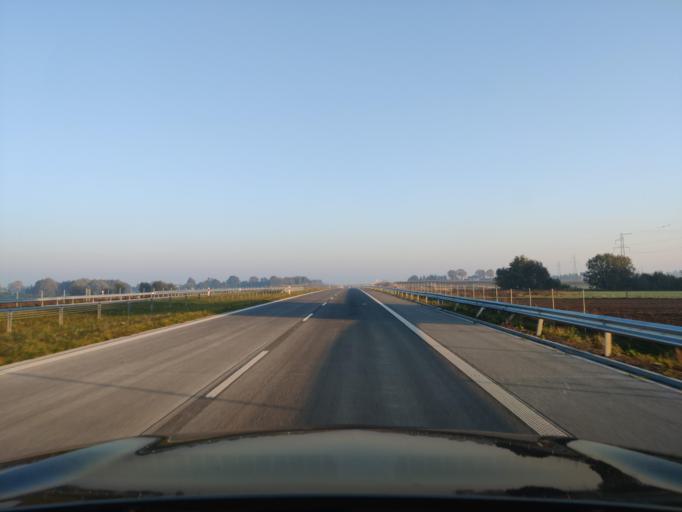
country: PL
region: Masovian Voivodeship
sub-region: Powiat mlawski
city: Mlawa
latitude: 53.1093
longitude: 20.4116
